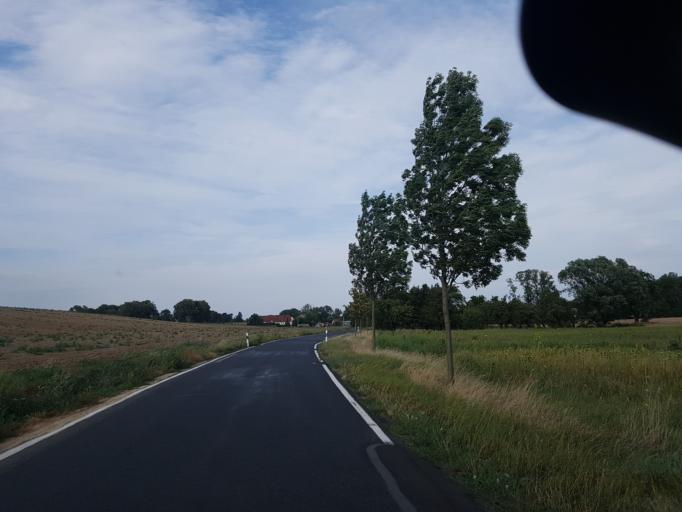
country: DE
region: Saxony
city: Ostrau
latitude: 51.2209
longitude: 13.1741
